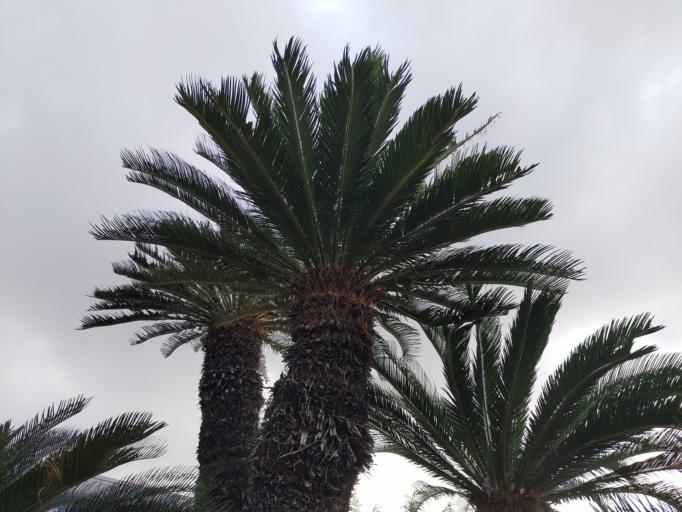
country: MY
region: Johor
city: Kampung Pasir Gudang Baru
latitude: 1.3660
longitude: 103.9882
